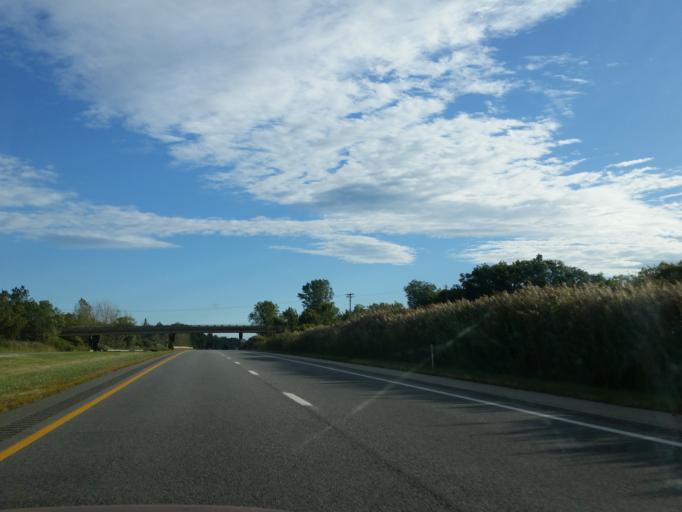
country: US
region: Pennsylvania
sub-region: Erie County
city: North East
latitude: 42.1997
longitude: -79.8160
